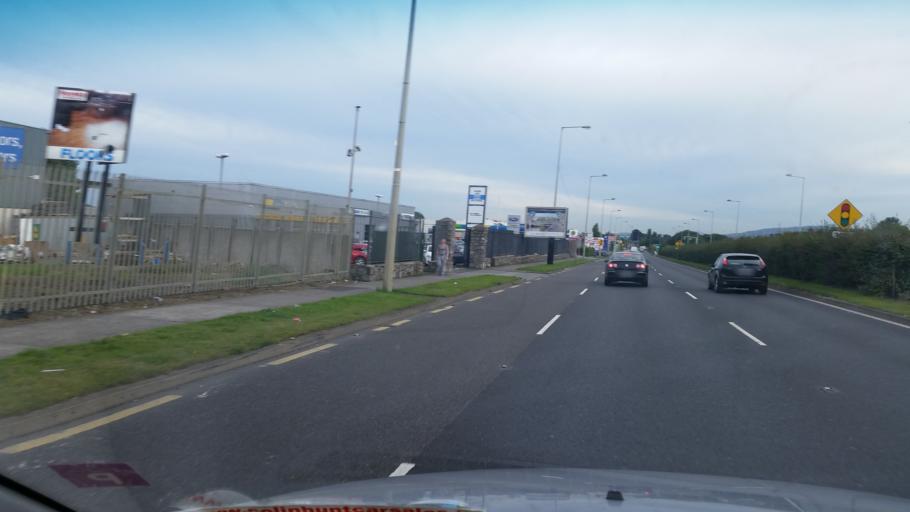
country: IE
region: Leinster
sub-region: Dublin City
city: Finglas
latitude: 53.4008
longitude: -6.3085
